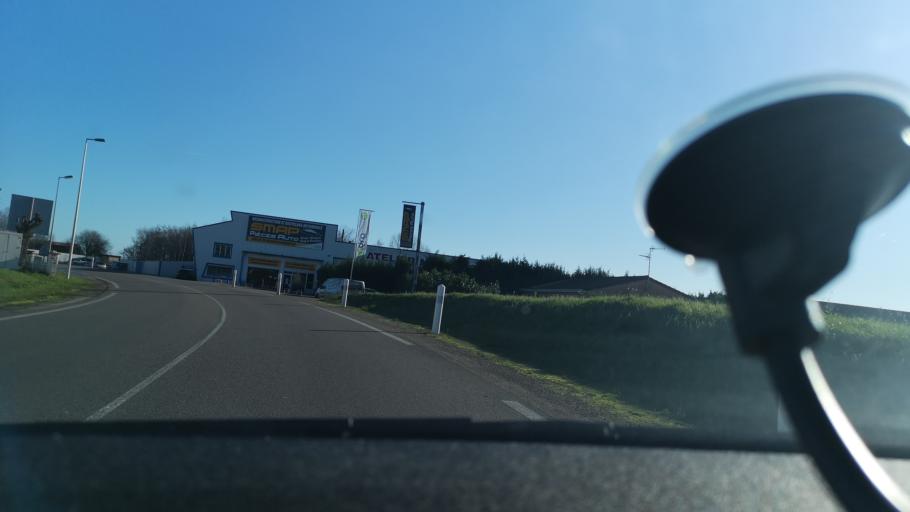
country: FR
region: Bourgogne
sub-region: Departement de Saone-et-Loire
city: Saint-Marcel
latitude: 46.7831
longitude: 4.9101
